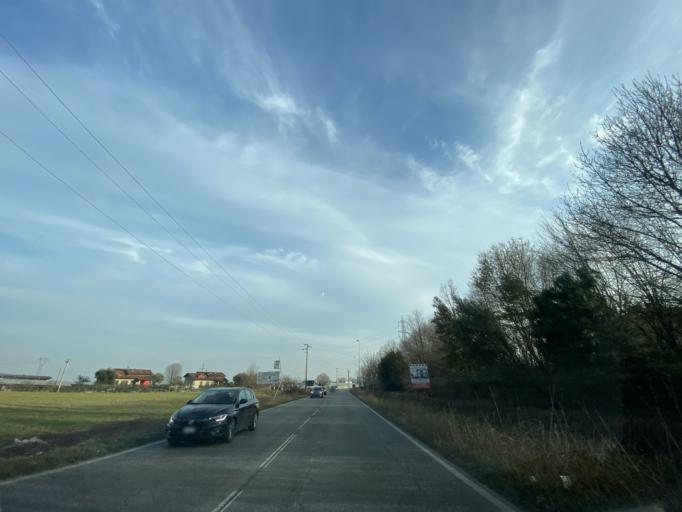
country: IT
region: Lombardy
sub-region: Citta metropolitana di Milano
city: Ronco
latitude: 45.5324
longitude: 9.3464
